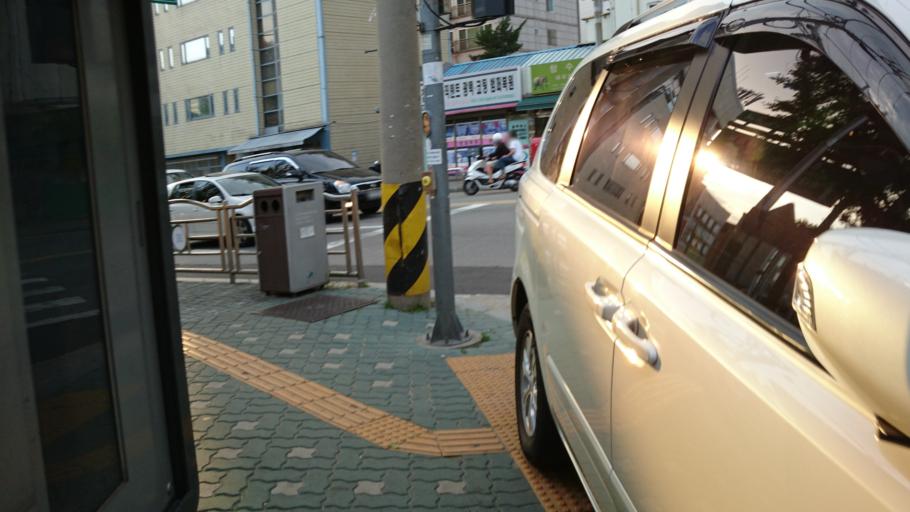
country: KR
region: Seoul
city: Seoul
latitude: 37.5458
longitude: 126.9784
